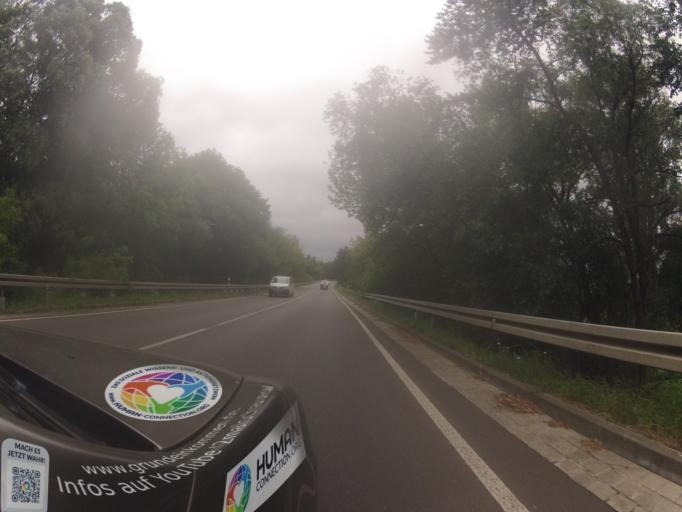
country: DE
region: Mecklenburg-Vorpommern
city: Pasewalk
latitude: 53.4885
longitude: 13.9827
